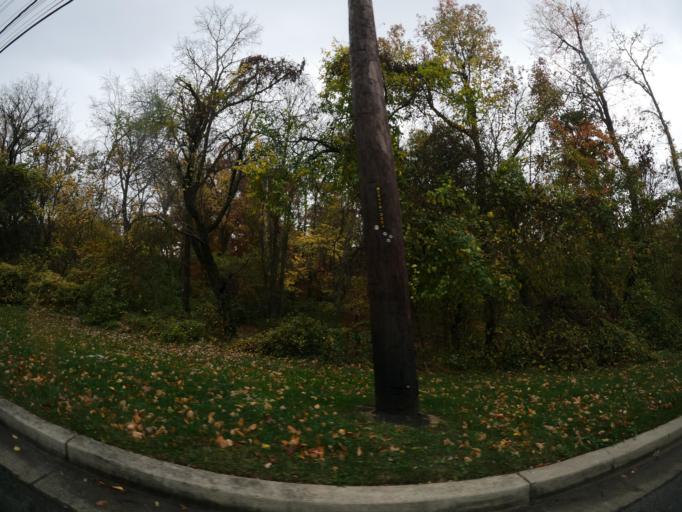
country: US
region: Maryland
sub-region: Prince George's County
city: College Park
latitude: 38.9813
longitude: -76.9459
